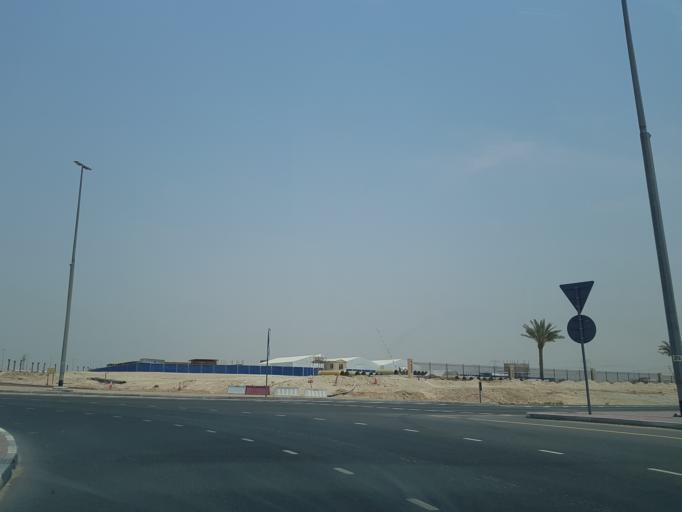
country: AE
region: Dubai
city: Dubai
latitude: 25.0073
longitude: 55.2552
